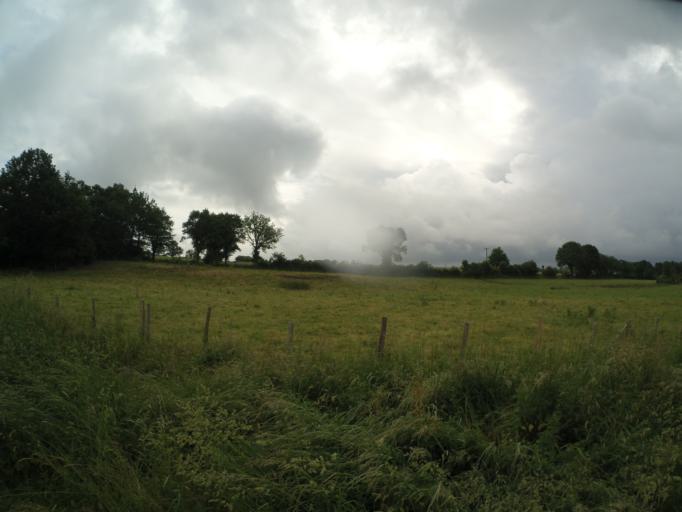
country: FR
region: Pays de la Loire
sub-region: Departement de la Vendee
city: Nesmy
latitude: 46.6132
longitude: -1.4001
